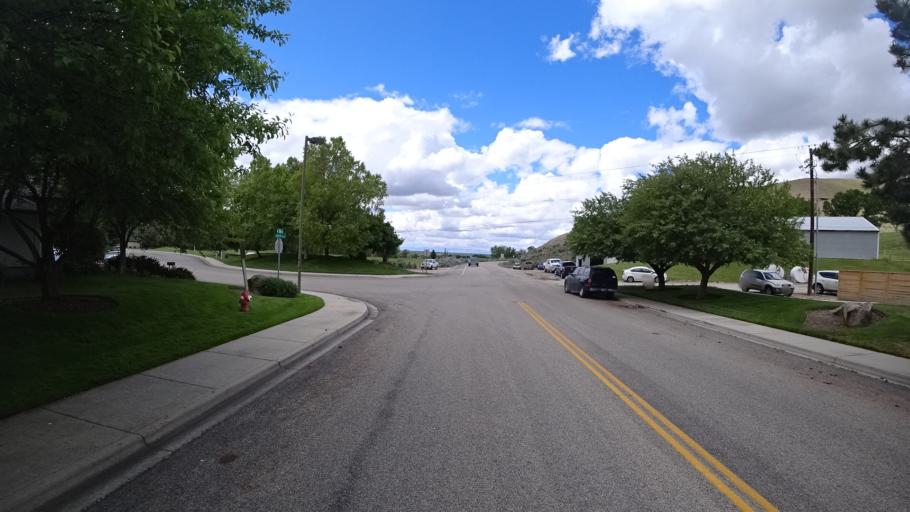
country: US
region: Idaho
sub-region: Ada County
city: Garden City
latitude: 43.6650
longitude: -116.2179
